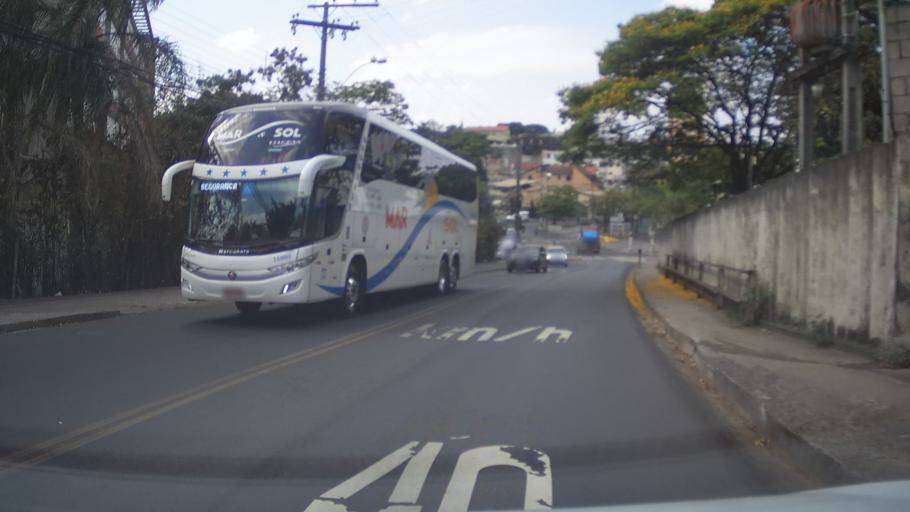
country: BR
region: Minas Gerais
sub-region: Belo Horizonte
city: Belo Horizonte
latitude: -19.8708
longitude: -43.9496
